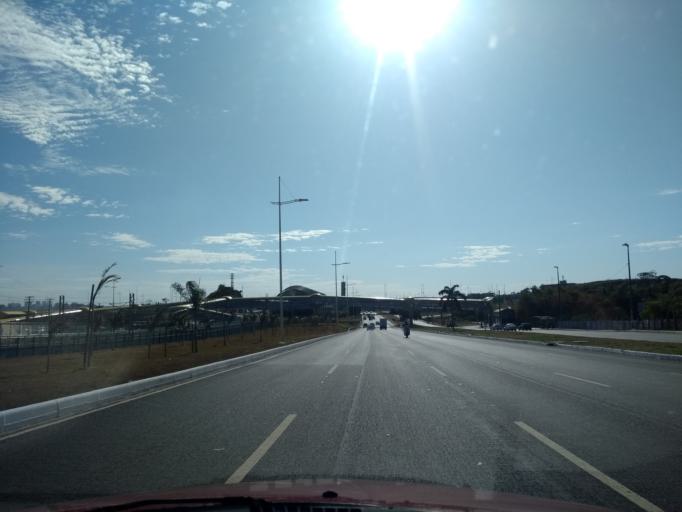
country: BR
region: Bahia
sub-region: Lauro De Freitas
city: Lauro de Freitas
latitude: -12.9248
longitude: -38.3782
